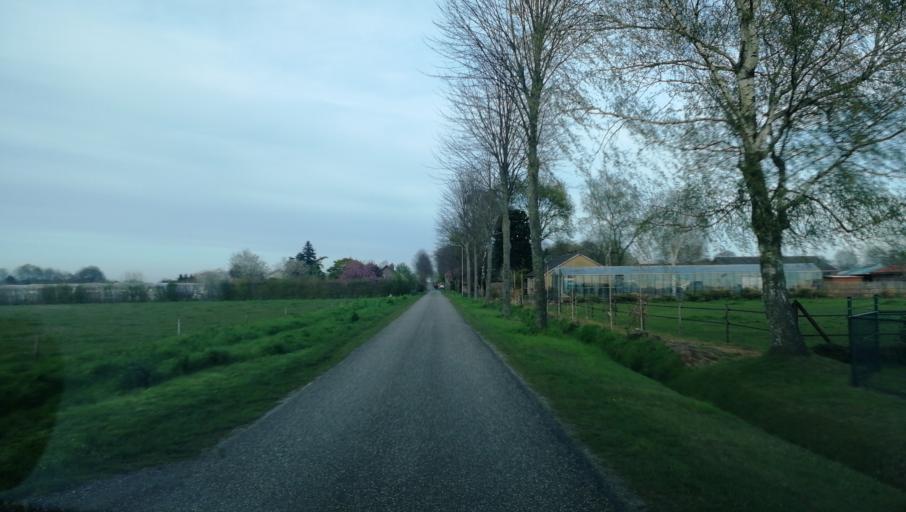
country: NL
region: Limburg
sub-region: Gemeente Peel en Maas
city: Maasbree
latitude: 51.4419
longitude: 6.0216
